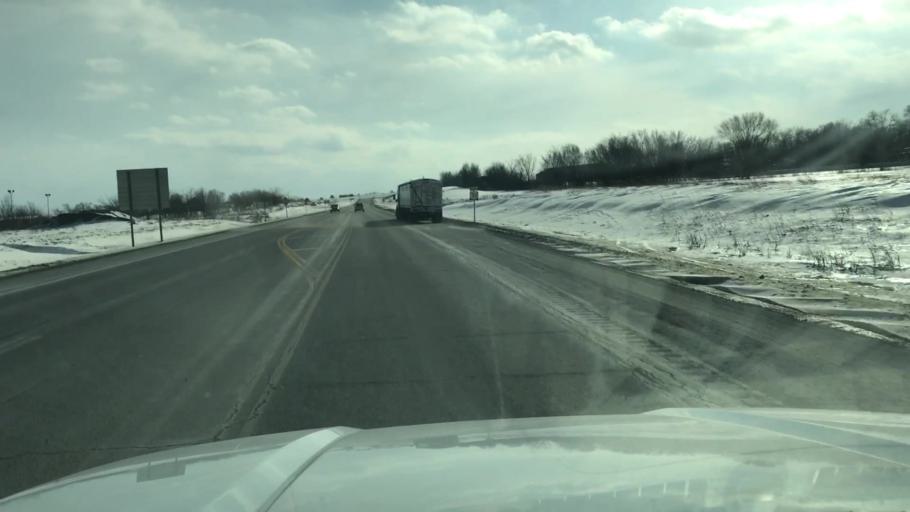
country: US
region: Missouri
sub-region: Nodaway County
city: Maryville
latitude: 40.3445
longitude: -94.8523
